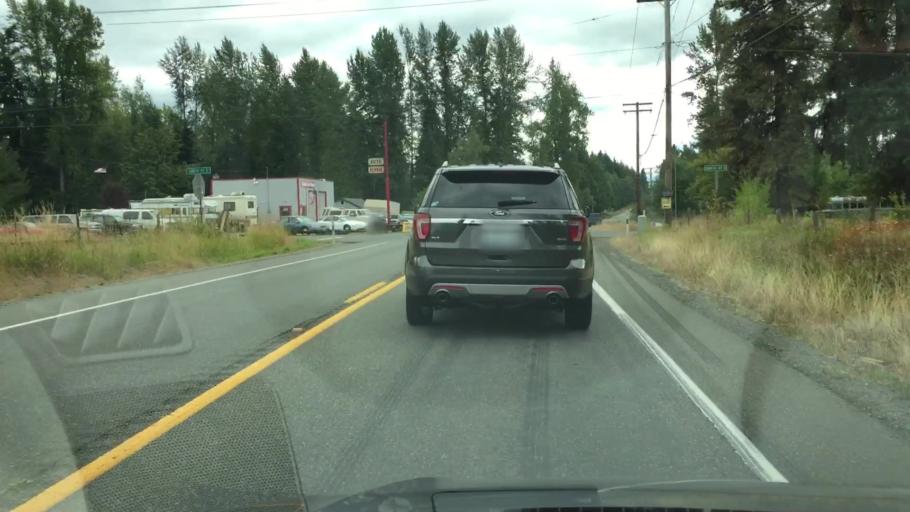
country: US
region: Washington
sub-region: Pierce County
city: Graham
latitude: 46.9953
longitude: -122.2956
